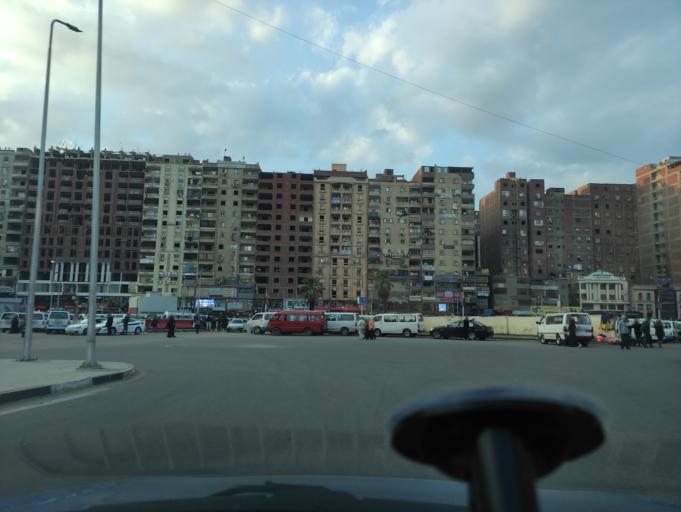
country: EG
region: Muhafazat al Qalyubiyah
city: Al Khankah
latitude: 30.1184
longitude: 31.3408
